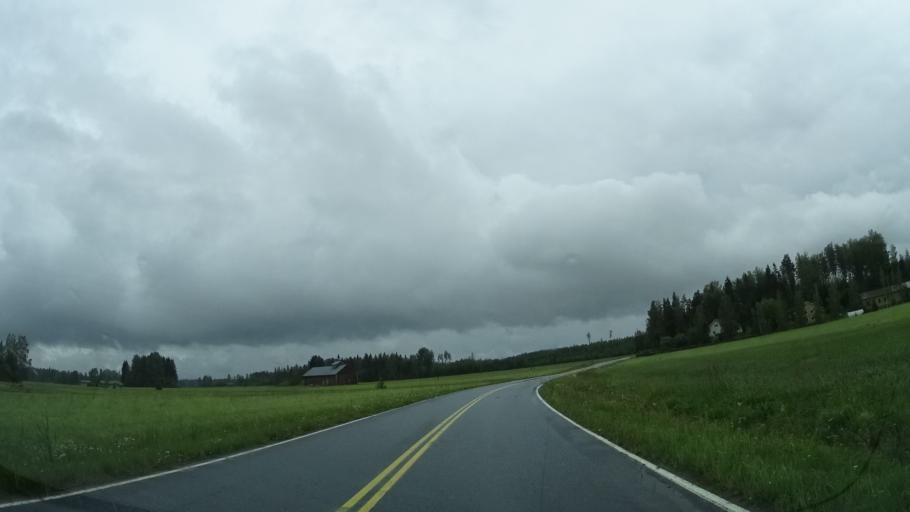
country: FI
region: Haeme
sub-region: Forssa
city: Humppila
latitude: 60.9945
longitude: 23.2542
